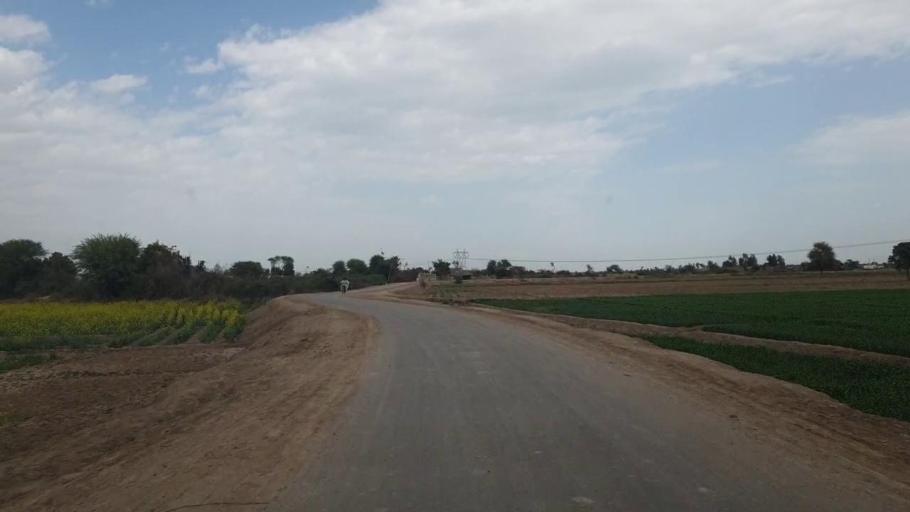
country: PK
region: Sindh
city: Hala
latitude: 25.9773
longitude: 68.4057
